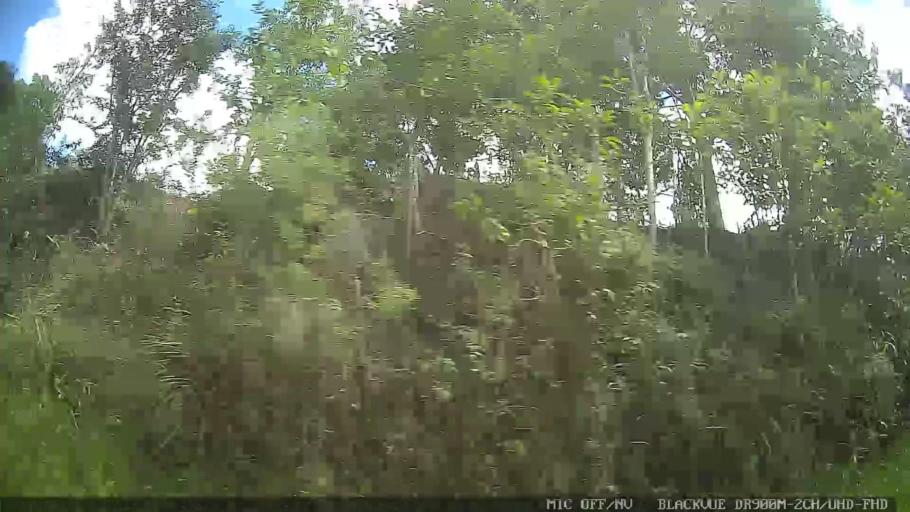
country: BR
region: Sao Paulo
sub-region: Caraguatatuba
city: Caraguatatuba
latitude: -23.5480
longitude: -45.5981
